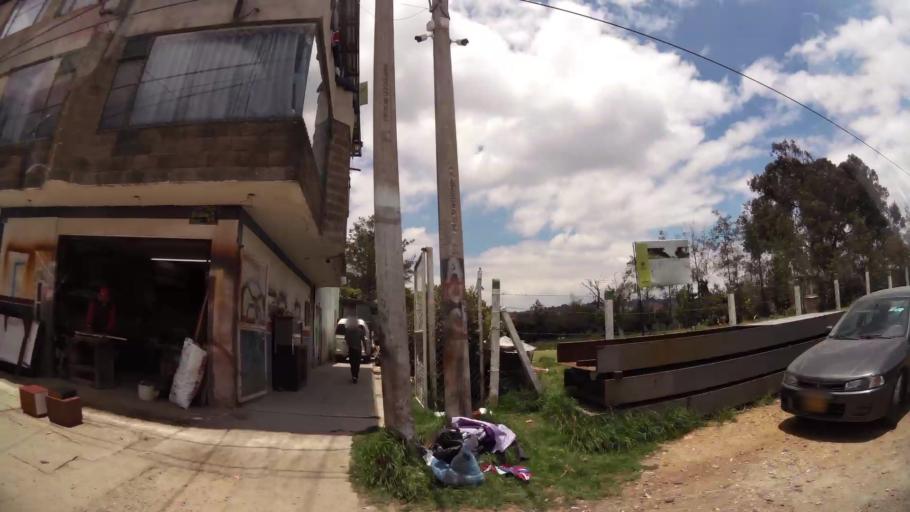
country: CO
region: Bogota D.C.
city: Barrio San Luis
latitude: 4.7134
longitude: -74.0641
